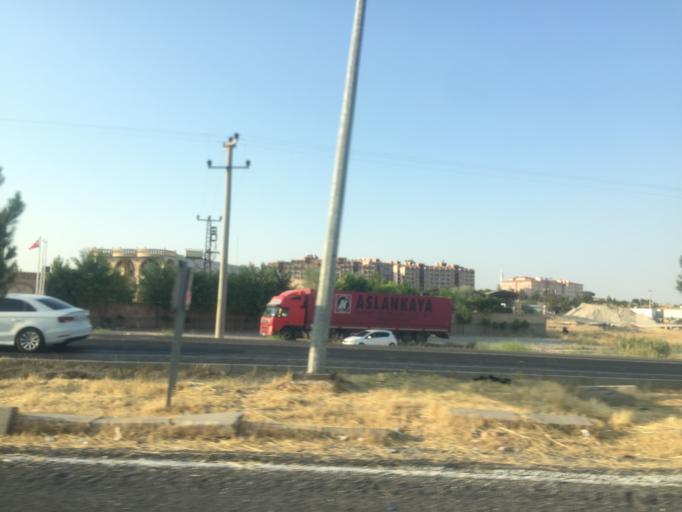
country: TR
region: Mardin
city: Acirli
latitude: 37.4369
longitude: 41.3143
